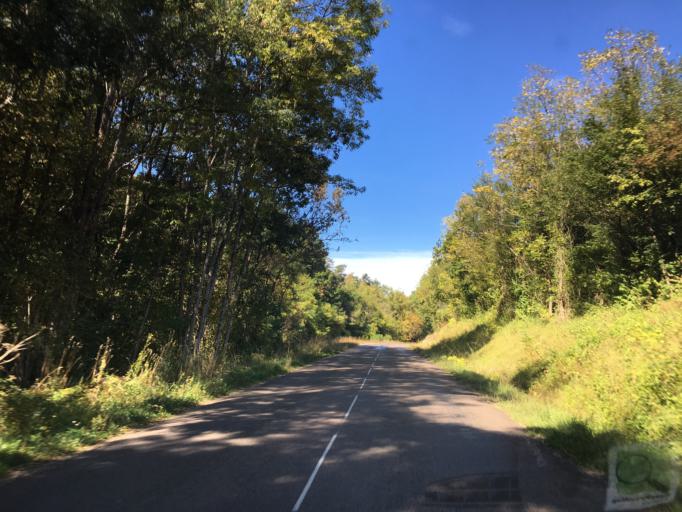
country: FR
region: Bourgogne
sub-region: Departement de l'Yonne
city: Vermenton
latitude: 47.5914
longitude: 3.6875
